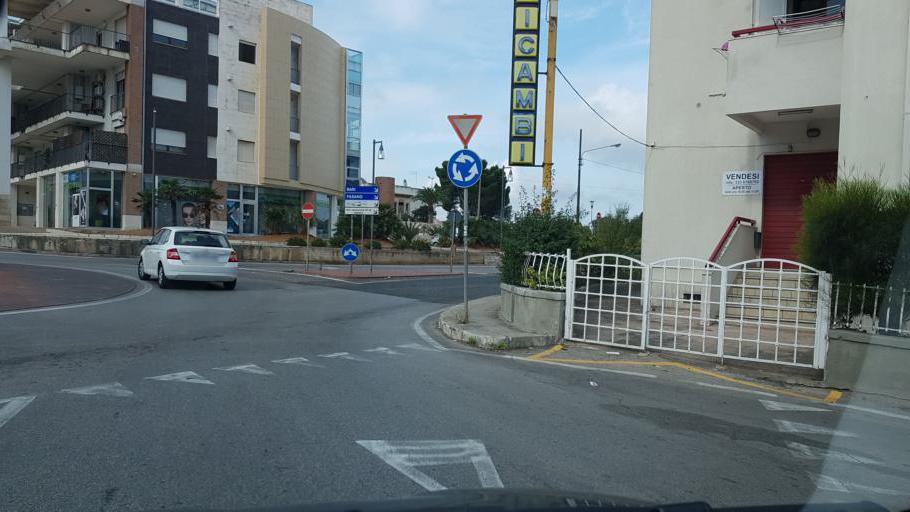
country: IT
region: Apulia
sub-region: Provincia di Brindisi
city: Ostuni
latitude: 40.7283
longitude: 17.5730
